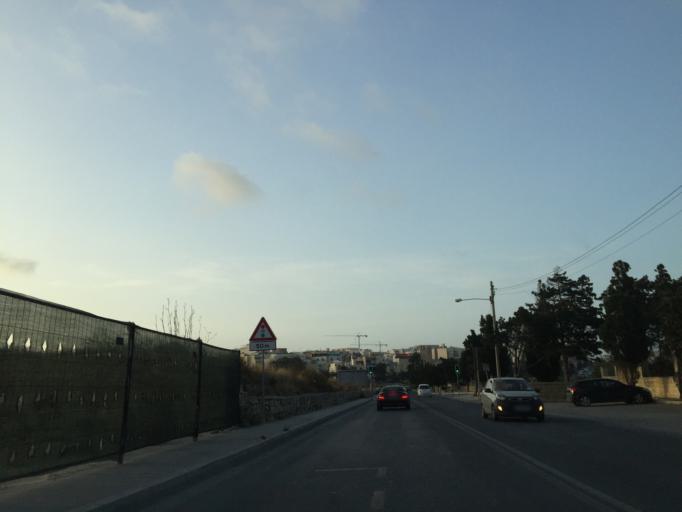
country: MT
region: Saint Paul's Bay
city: San Pawl il-Bahar
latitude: 35.9414
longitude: 14.4115
